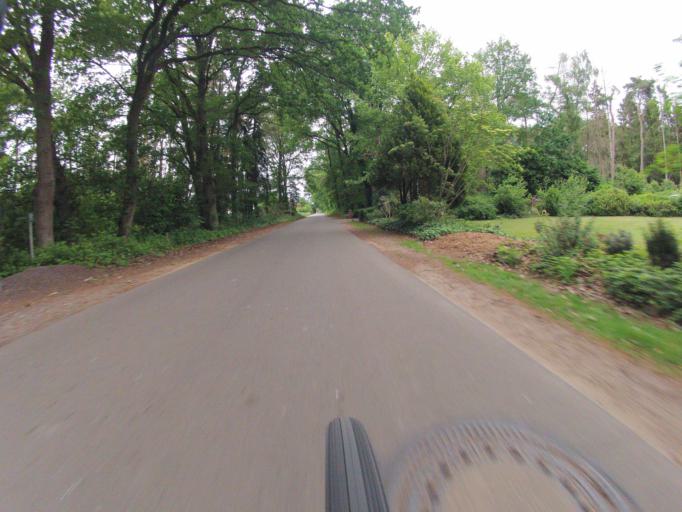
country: DE
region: North Rhine-Westphalia
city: Emsdetten
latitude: 52.2308
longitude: 7.5164
